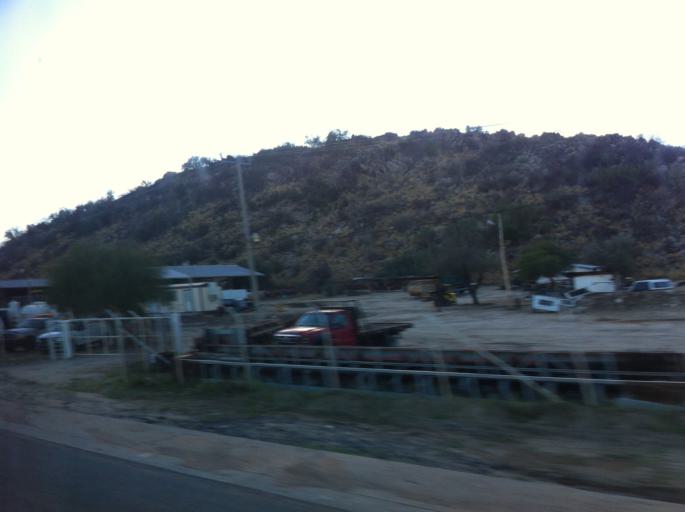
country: MX
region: Sonora
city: Hermosillo
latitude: 29.1463
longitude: -110.9097
